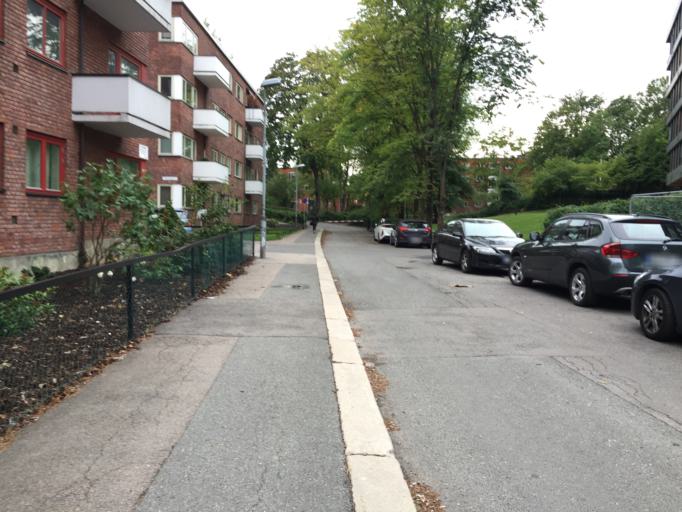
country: NO
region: Oslo
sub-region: Oslo
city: Oslo
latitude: 59.9137
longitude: 10.7189
